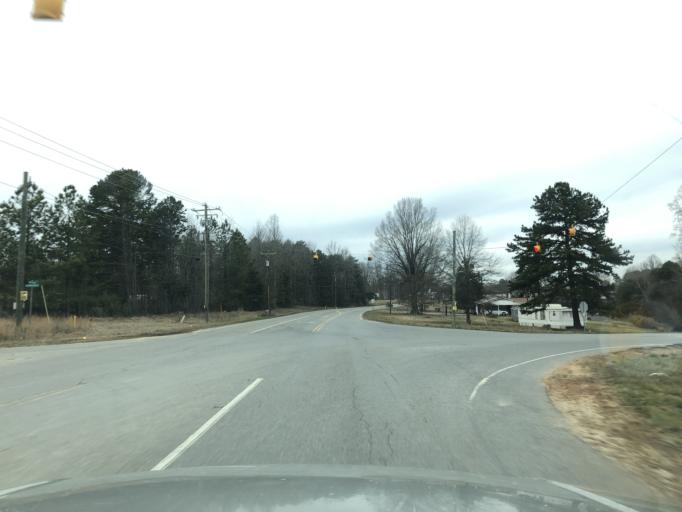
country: US
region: North Carolina
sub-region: Cleveland County
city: Shelby
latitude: 35.3198
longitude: -81.4957
